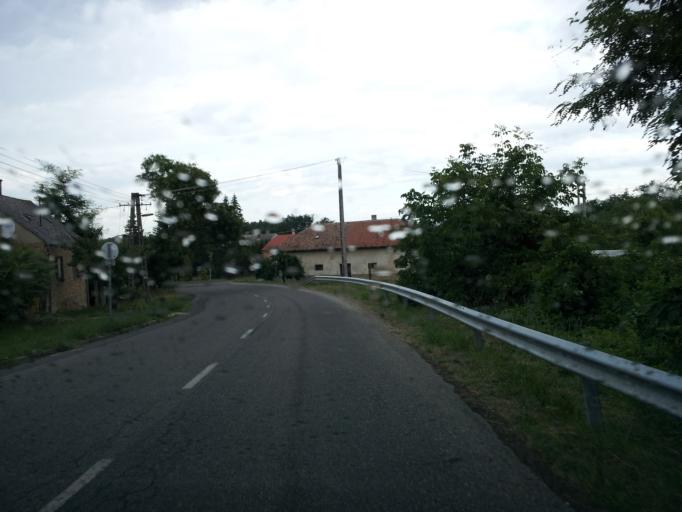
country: HU
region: Zala
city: Turje
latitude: 47.0854
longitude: 17.0240
